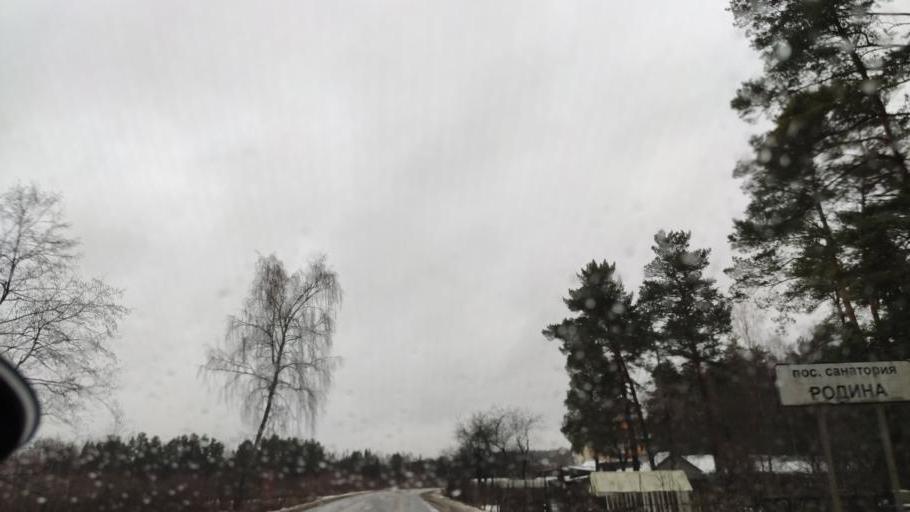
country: RU
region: Moskovskaya
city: Dubrovitsy
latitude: 55.4398
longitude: 37.3988
